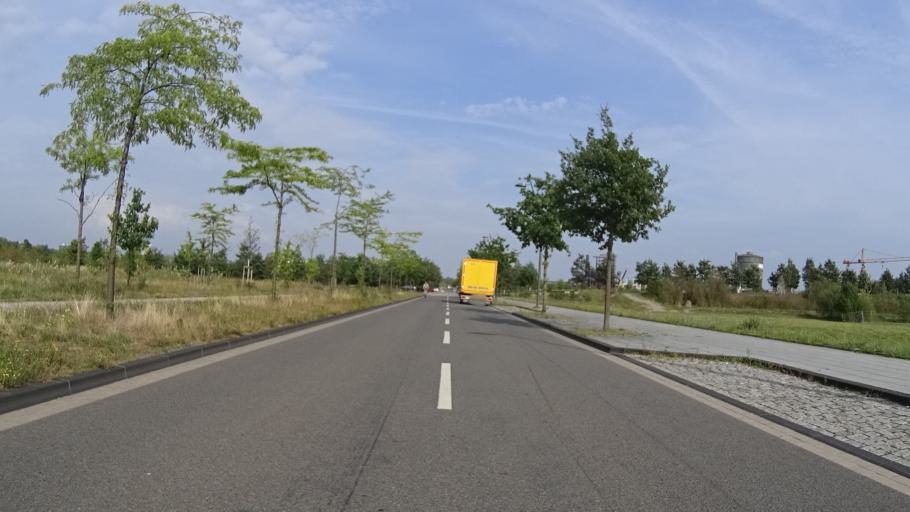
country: DE
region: North Rhine-Westphalia
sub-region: Regierungsbezirk Arnsberg
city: Dortmund
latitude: 51.4874
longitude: 7.4717
